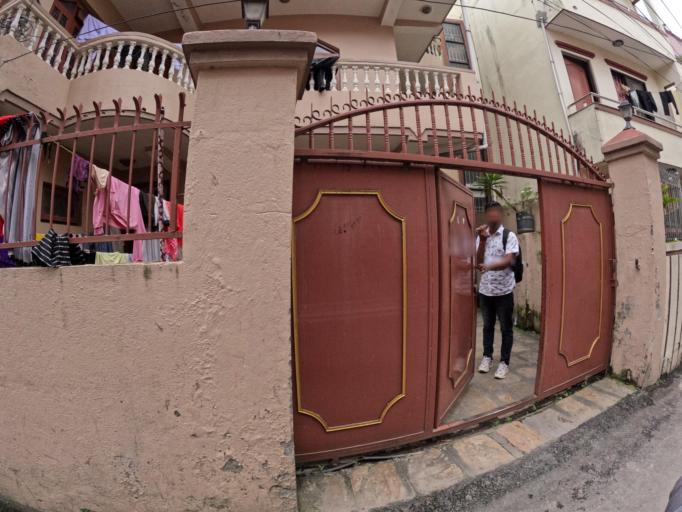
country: NP
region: Central Region
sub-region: Bagmati Zone
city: Kathmandu
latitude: 27.7430
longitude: 85.3213
